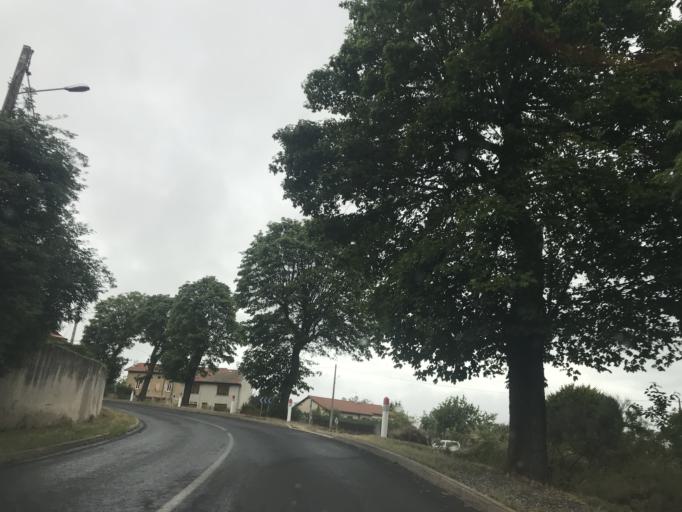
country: FR
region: Auvergne
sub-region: Departement de la Haute-Loire
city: Saint-Paulien
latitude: 45.2199
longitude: 3.8170
